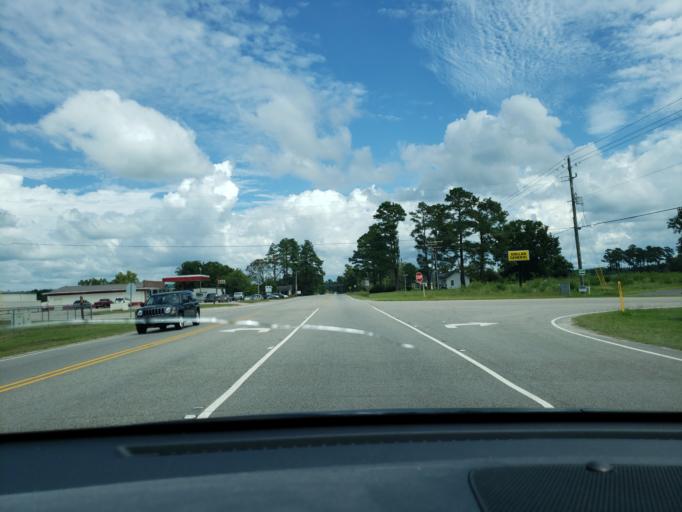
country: US
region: North Carolina
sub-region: Columbus County
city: Brunswick
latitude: 34.2040
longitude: -78.7630
